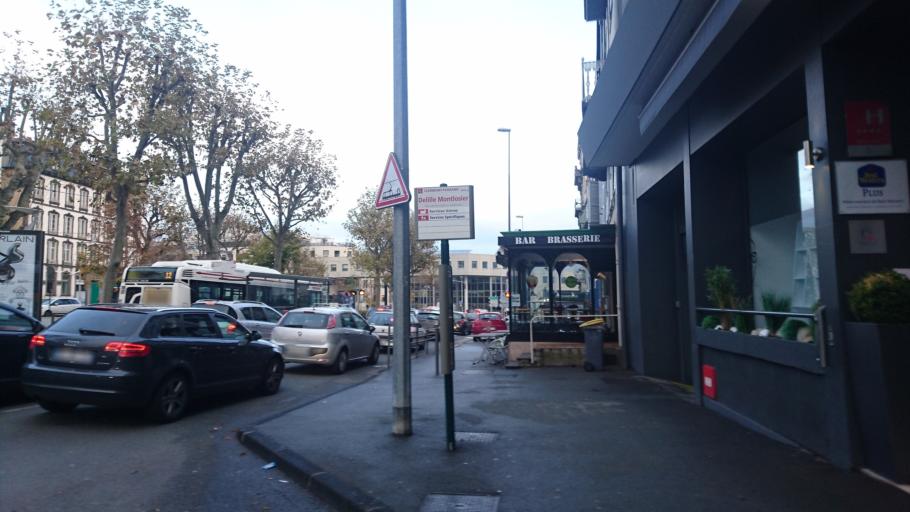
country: FR
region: Auvergne
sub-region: Departement du Puy-de-Dome
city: Clermont-Ferrand
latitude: 45.7802
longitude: 3.0916
